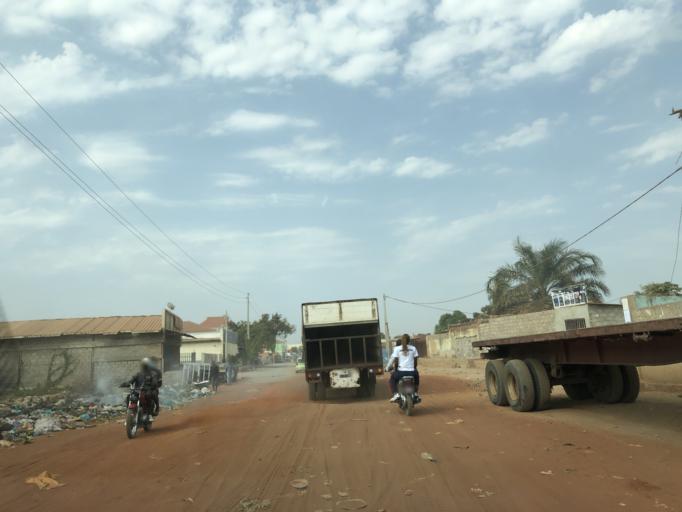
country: AO
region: Luanda
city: Luanda
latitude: -8.8959
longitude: 13.3519
